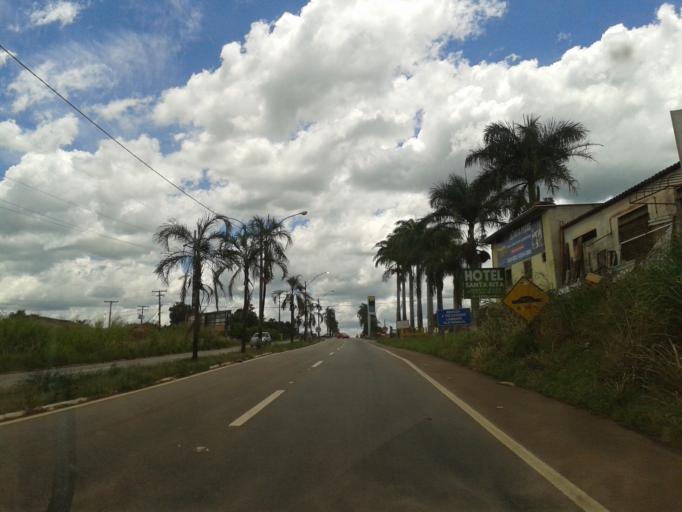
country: BR
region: Goias
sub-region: Petrolina De Goias
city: Petrolina de Goias
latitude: -16.1032
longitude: -49.3332
